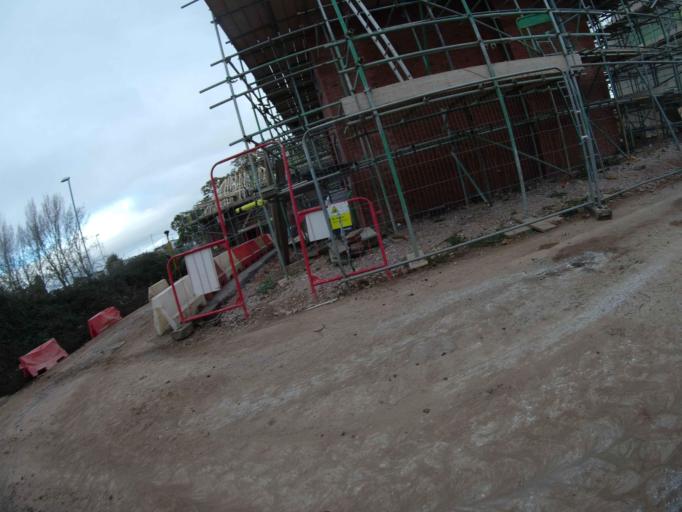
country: GB
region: England
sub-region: Devon
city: Topsham
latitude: 50.6983
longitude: -3.4795
